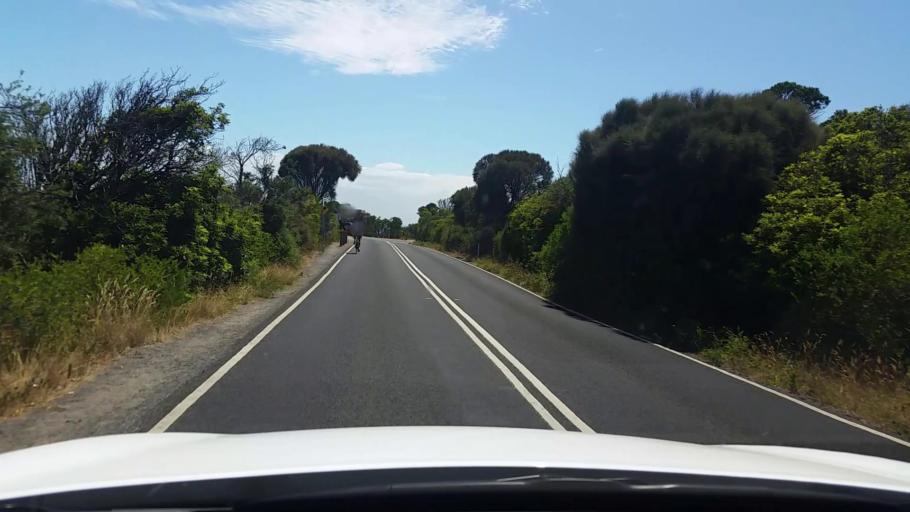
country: AU
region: Victoria
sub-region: Mornington Peninsula
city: Mount Martha
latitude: -38.2725
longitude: 145.0017
